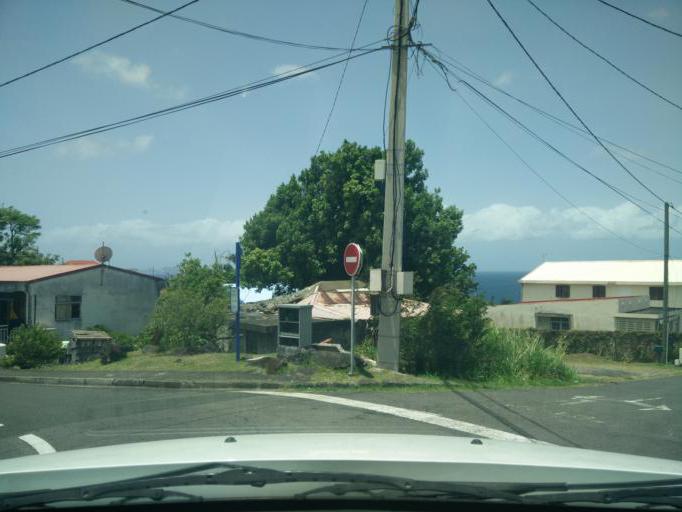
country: GP
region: Guadeloupe
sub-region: Guadeloupe
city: Gourbeyre
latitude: 15.9494
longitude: -61.6992
